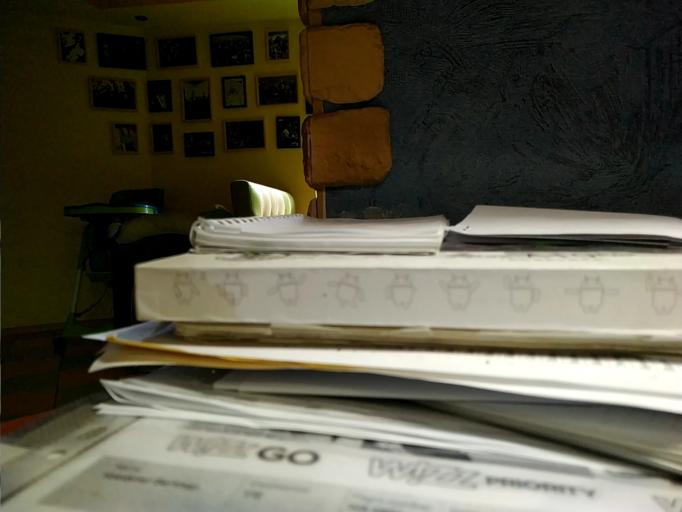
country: RU
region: Novgorod
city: Poddor'ye
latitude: 57.5415
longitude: 30.8882
